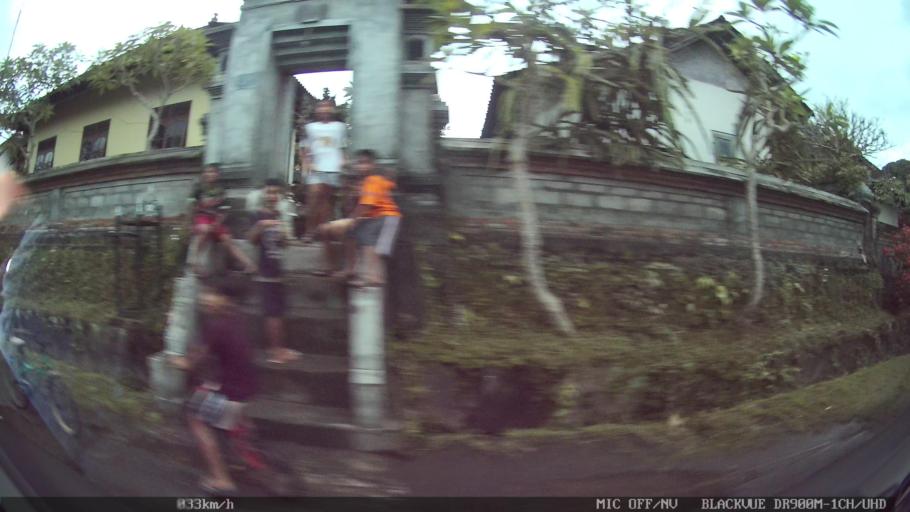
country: ID
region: Bali
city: Banjar Tebongkang
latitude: -8.5290
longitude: 115.2370
